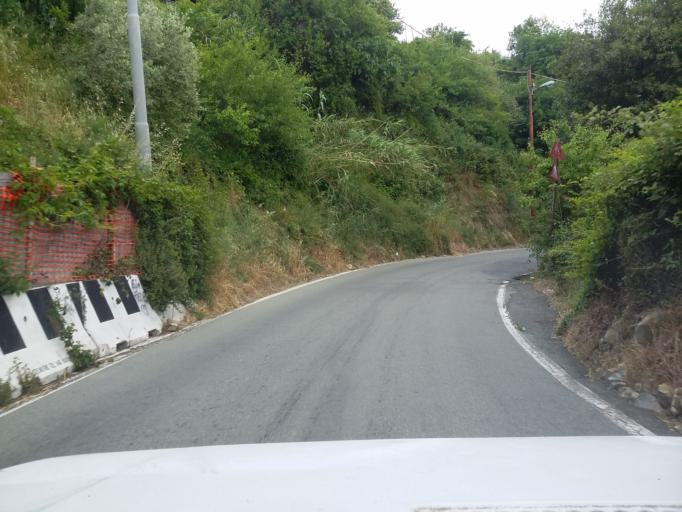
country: IT
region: Liguria
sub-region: Provincia di Genova
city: Piccarello
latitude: 44.4171
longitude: 8.9844
